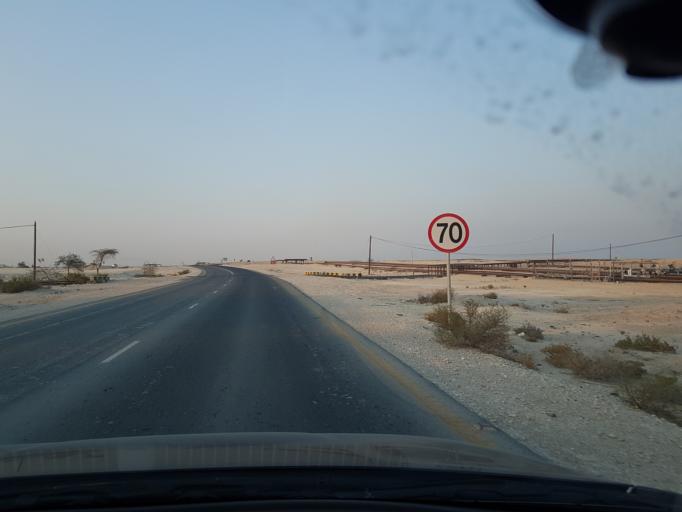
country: BH
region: Central Governorate
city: Dar Kulayb
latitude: 26.0443
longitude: 50.5567
